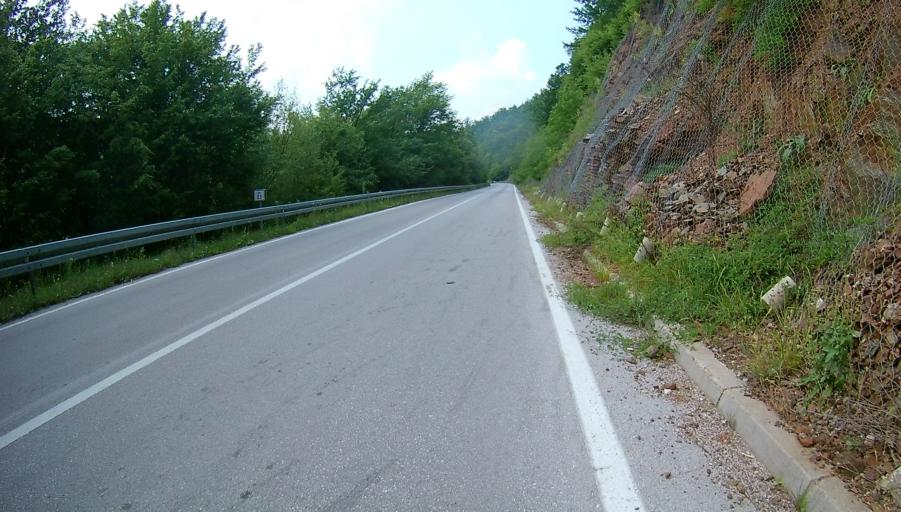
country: RS
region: Central Serbia
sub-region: Nisavski Okrug
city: Gadzin Han
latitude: 43.1825
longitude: 22.0301
